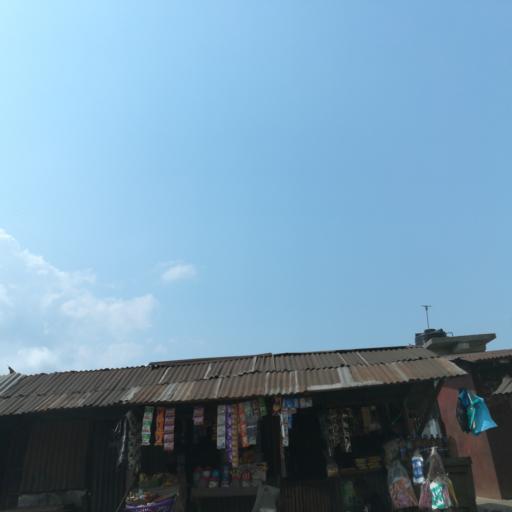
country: NG
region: Rivers
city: Okrika
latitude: 4.7950
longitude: 7.1137
